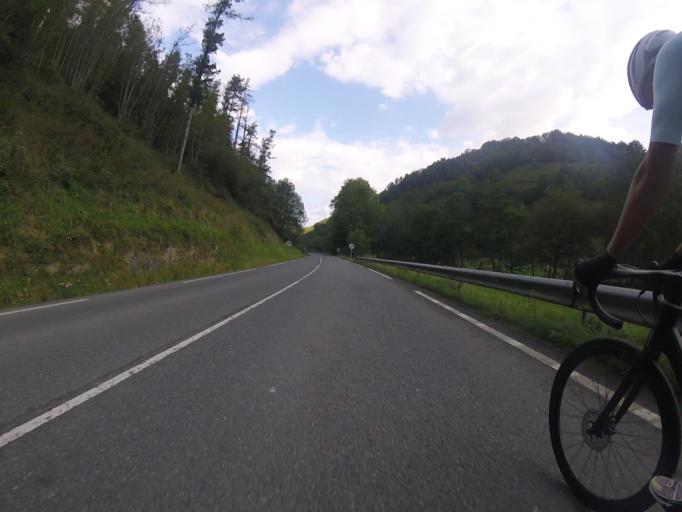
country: ES
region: Basque Country
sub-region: Provincia de Guipuzcoa
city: Amezqueta
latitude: 43.0697
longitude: -2.0843
